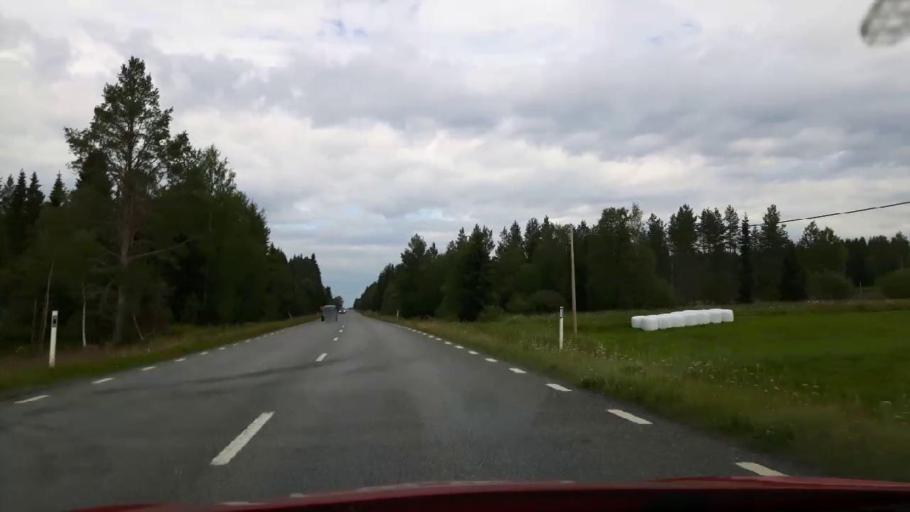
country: SE
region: Jaemtland
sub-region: Stroemsunds Kommun
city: Stroemsund
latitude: 63.5582
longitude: 15.3718
